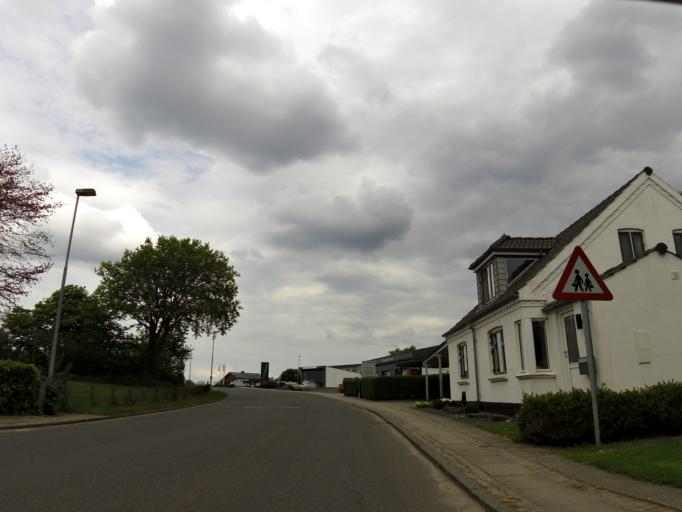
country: DK
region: Central Jutland
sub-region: Holstebro Kommune
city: Vinderup
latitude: 56.5232
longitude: 8.7860
